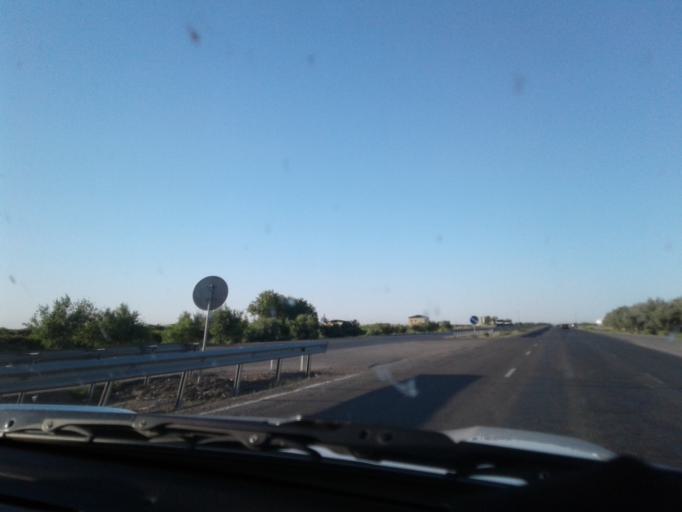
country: TM
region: Mary
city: Mary
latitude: 37.4905
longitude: 61.6994
